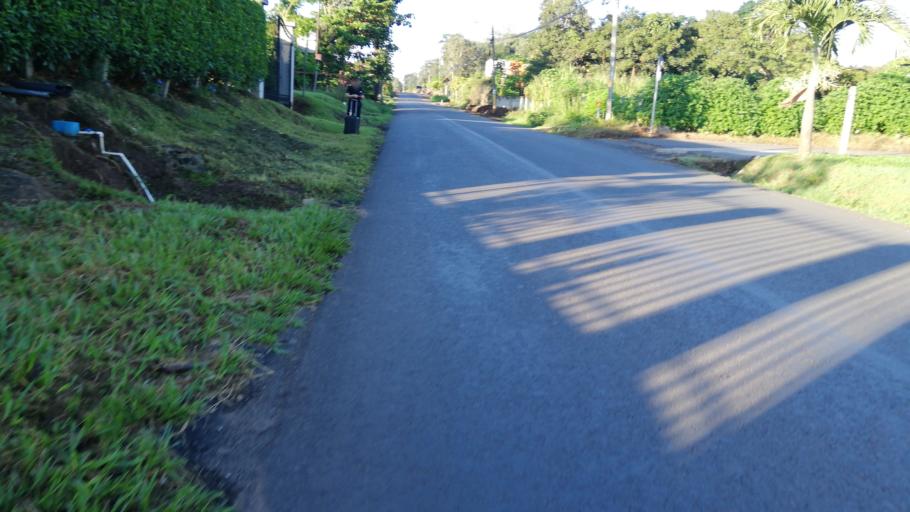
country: CR
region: Alajuela
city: Atenas
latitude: 10.0006
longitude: -84.3813
